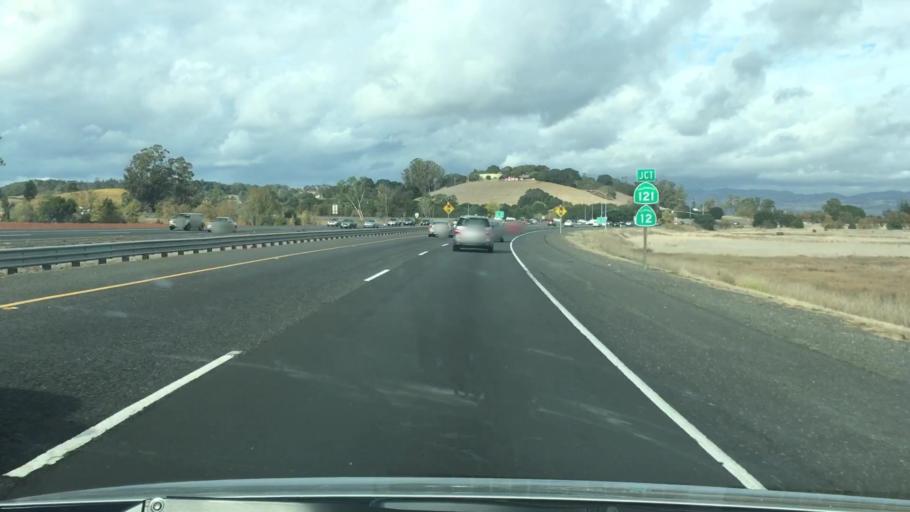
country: US
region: California
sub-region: Napa County
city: Napa
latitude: 38.2537
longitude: -122.3033
